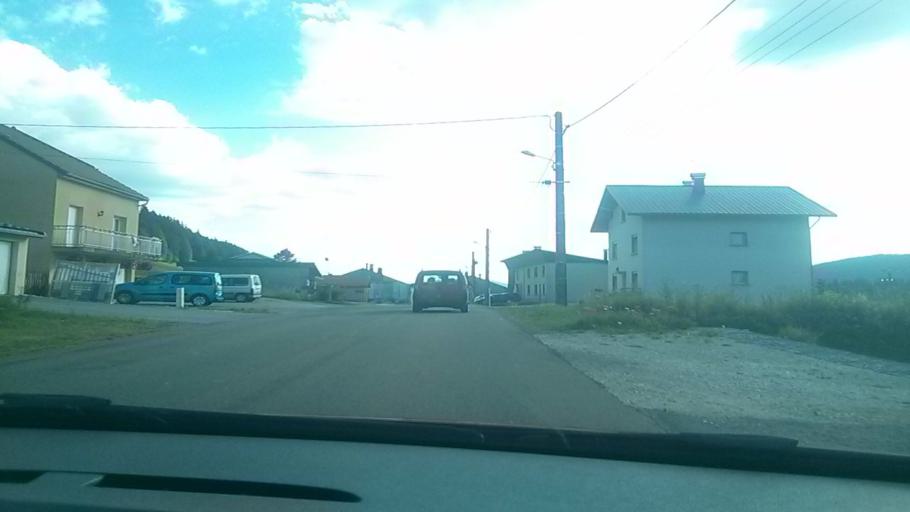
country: FR
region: Franche-Comte
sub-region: Departement du Jura
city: Les Rousses
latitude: 46.5200
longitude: 6.1220
